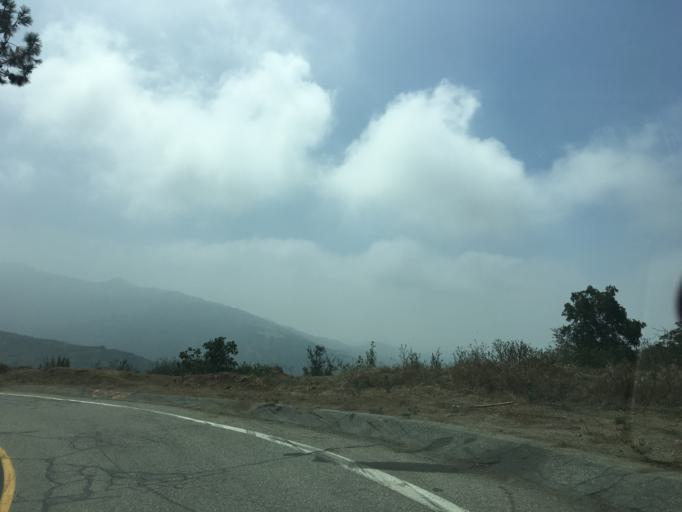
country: US
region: California
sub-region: Los Angeles County
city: Glendora
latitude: 34.1668
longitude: -117.8478
